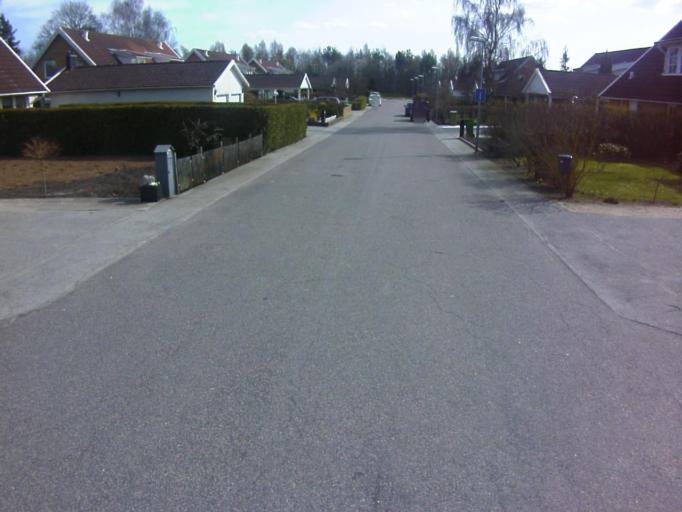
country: SE
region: Skane
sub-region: Kavlinge Kommun
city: Kaevlinge
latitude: 55.8046
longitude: 13.1118
